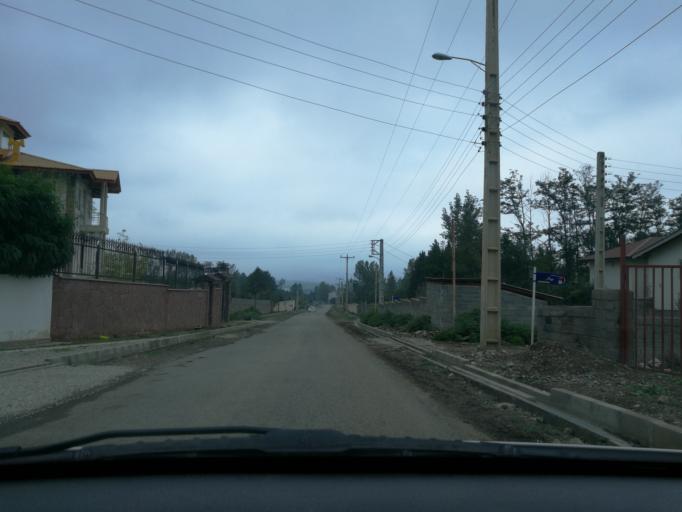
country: IR
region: Mazandaran
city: `Abbasabad
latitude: 36.4981
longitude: 51.2164
